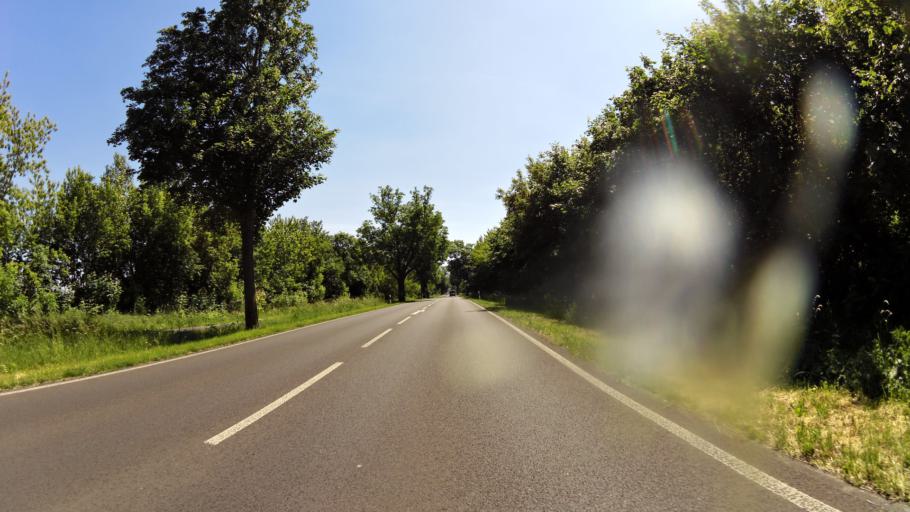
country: DE
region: Brandenburg
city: Lebus
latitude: 52.3832
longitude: 14.5190
